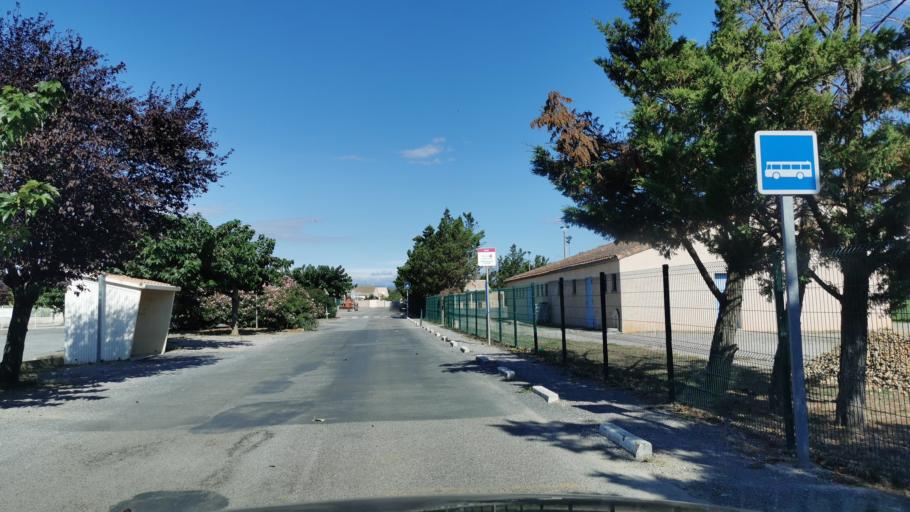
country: FR
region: Languedoc-Roussillon
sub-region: Departement de l'Aude
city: Ginestas
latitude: 43.2451
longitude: 2.8896
